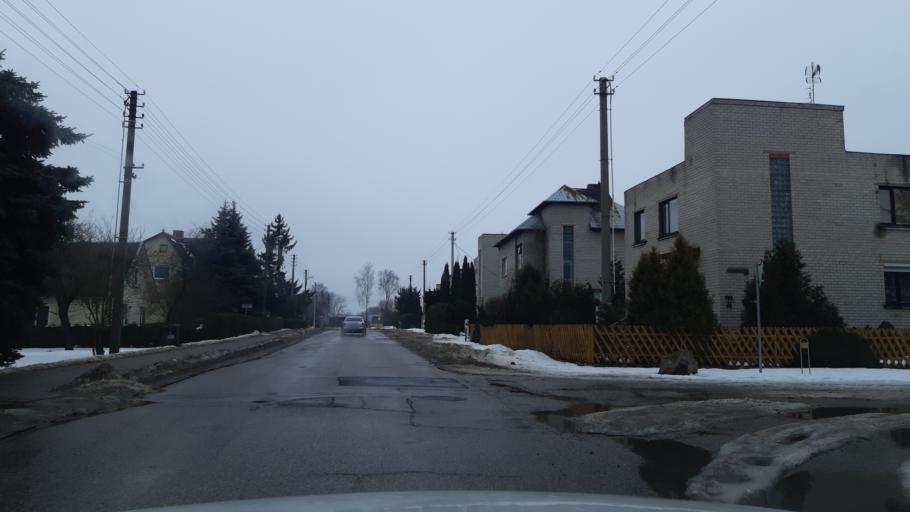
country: LT
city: Vilkaviskis
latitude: 54.6464
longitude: 23.0198
